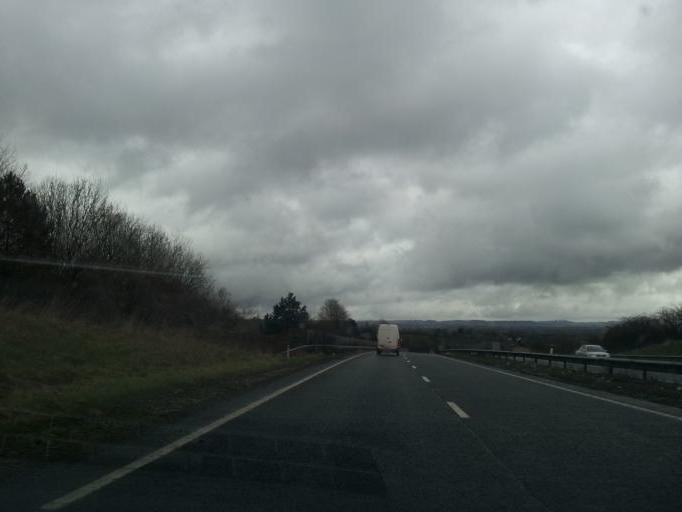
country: GB
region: England
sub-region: Somerset
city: Wincanton
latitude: 51.0686
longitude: -2.3485
